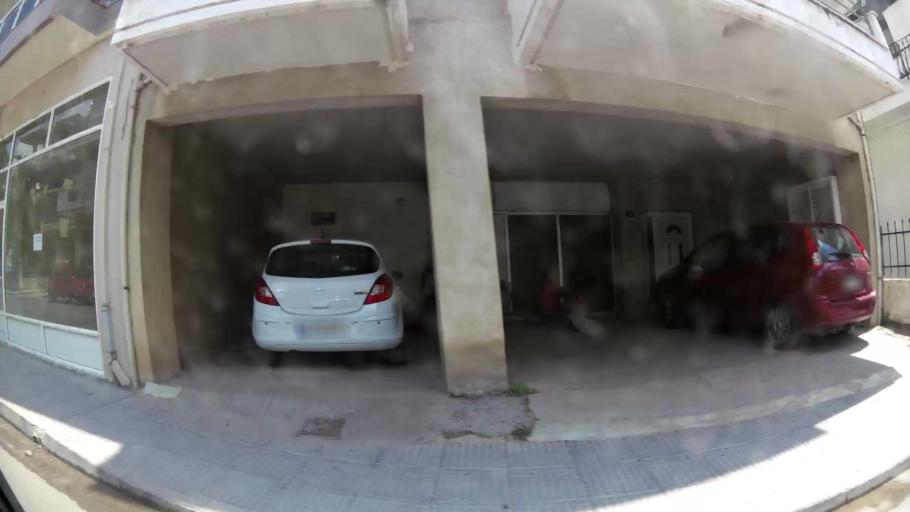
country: GR
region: West Macedonia
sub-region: Nomos Kozanis
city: Kozani
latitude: 40.2942
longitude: 21.7840
